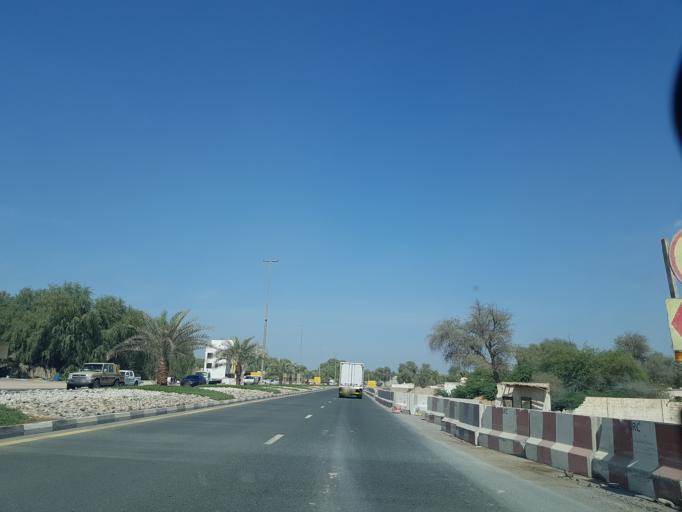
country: AE
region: Ra's al Khaymah
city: Ras al-Khaimah
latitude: 25.6948
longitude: 55.9678
